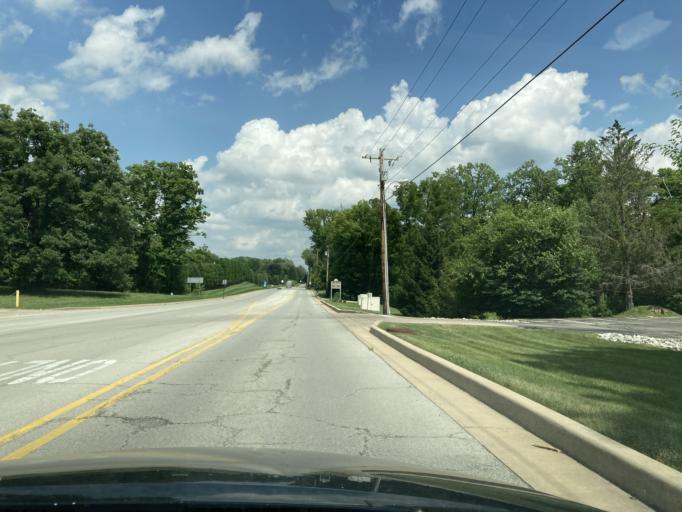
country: US
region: Indiana
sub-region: Boone County
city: Zionsville
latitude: 39.9553
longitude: -86.2419
